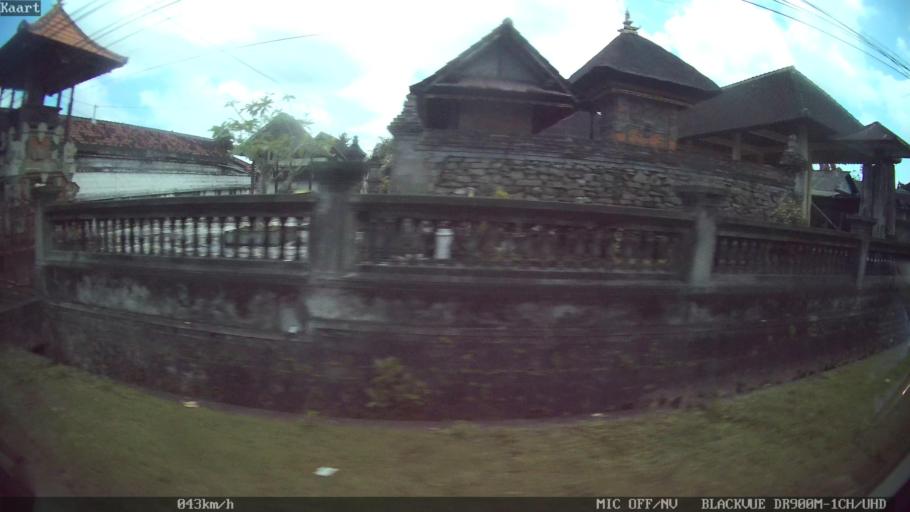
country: ID
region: Bali
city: Banjar Sedang
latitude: -8.5629
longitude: 115.2862
